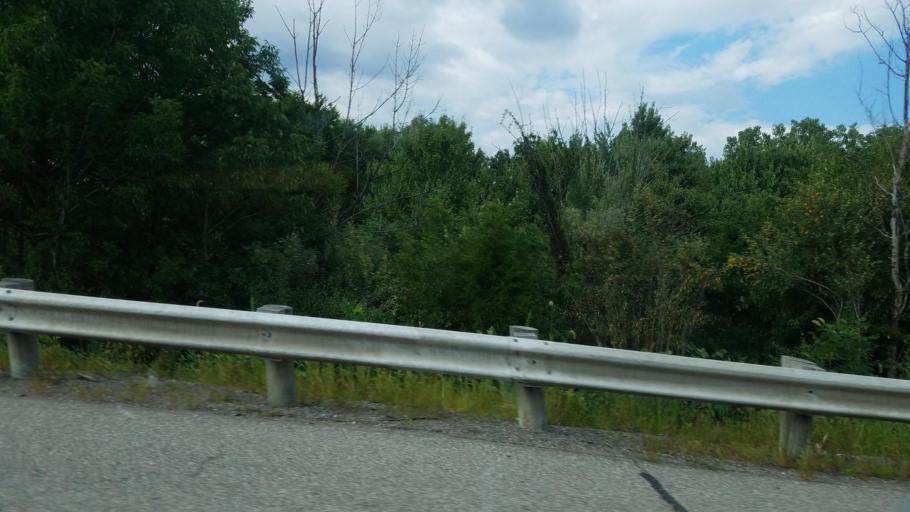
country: US
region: Ohio
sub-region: Trumbull County
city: Mineral Ridge
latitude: 41.1281
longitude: -80.7428
